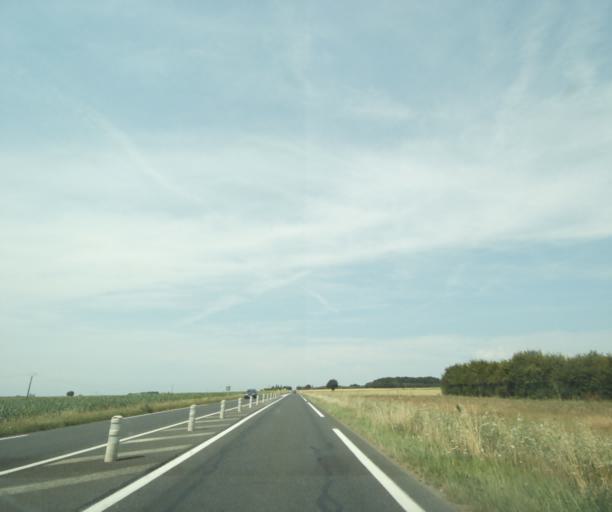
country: FR
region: Centre
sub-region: Departement d'Indre-et-Loire
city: Sainte-Maure-de-Touraine
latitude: 47.1621
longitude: 0.6489
